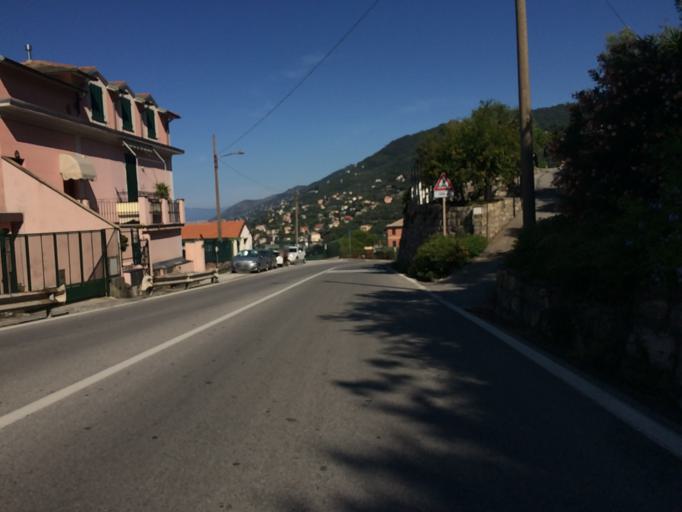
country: IT
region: Liguria
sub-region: Provincia di Genova
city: Recco
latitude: 44.3568
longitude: 9.1475
